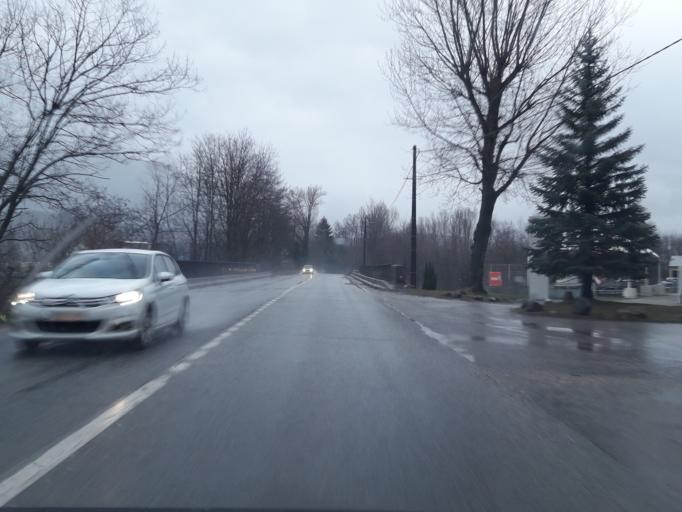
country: FR
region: Rhone-Alpes
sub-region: Departement de la Savoie
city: Le Bourget-du-Lac
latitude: 45.6399
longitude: 5.8681
